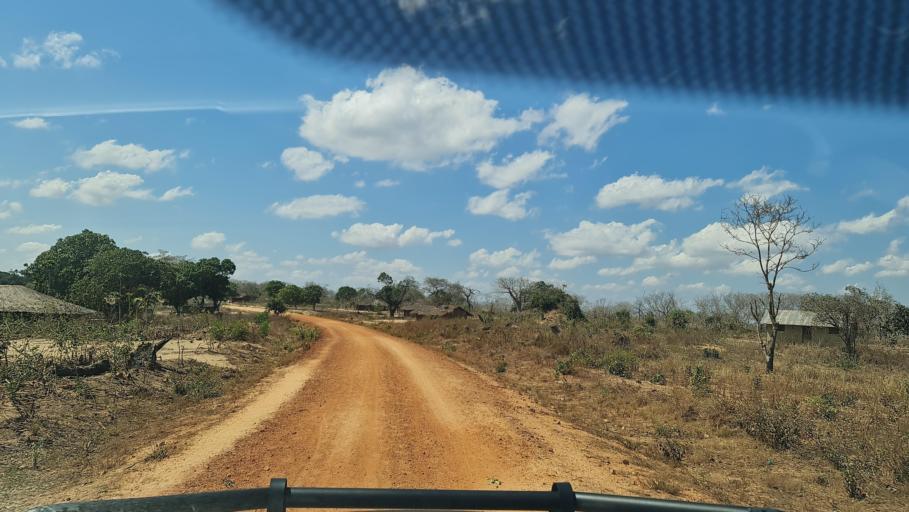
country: MZ
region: Nampula
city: Nacala
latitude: -14.1772
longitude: 40.2180
